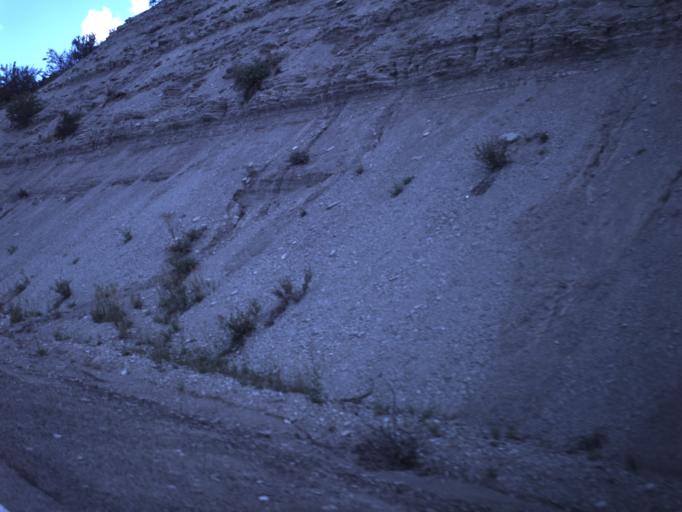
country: US
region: Utah
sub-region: Carbon County
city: Helper
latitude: 39.9008
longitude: -110.7440
